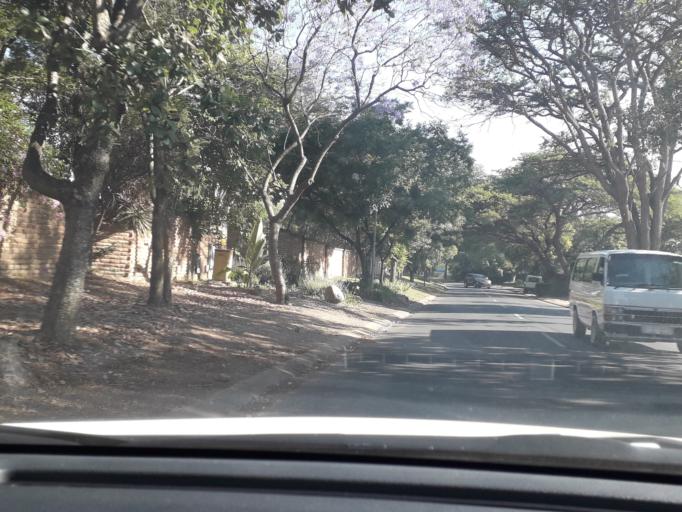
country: ZA
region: Gauteng
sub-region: City of Johannesburg Metropolitan Municipality
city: Diepsloot
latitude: -26.0384
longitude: 27.9852
